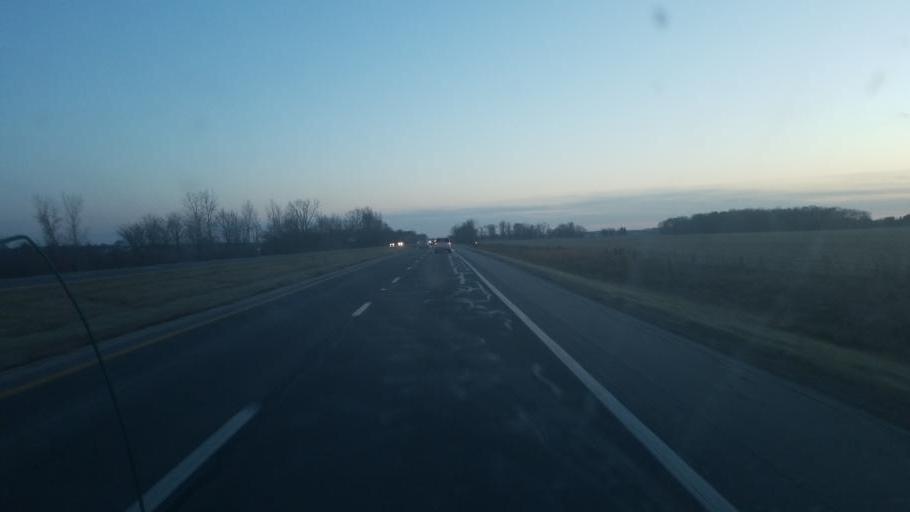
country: US
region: Ohio
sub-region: Marion County
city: Marion
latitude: 40.5089
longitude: -83.0749
